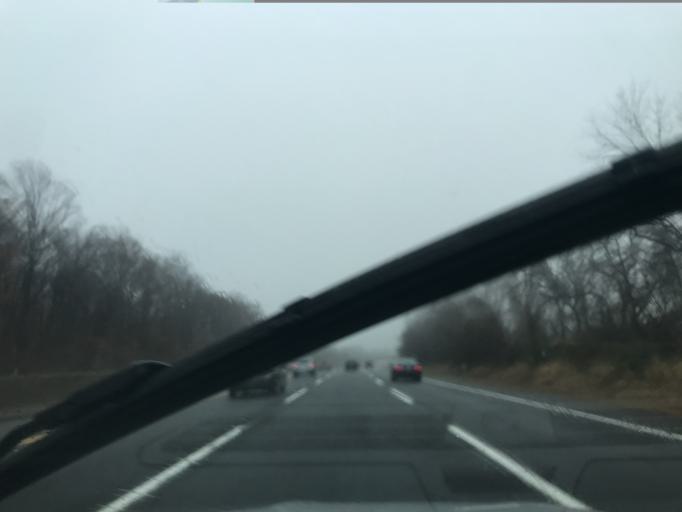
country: US
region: New Jersey
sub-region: Burlington County
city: Willingboro
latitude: 40.0130
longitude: -74.8354
